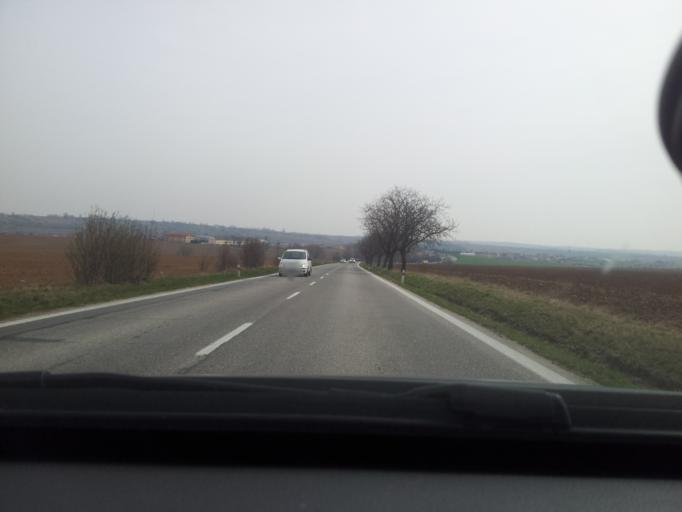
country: SK
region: Nitriansky
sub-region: Okres Nitra
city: Nitra
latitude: 48.3008
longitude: 18.1629
